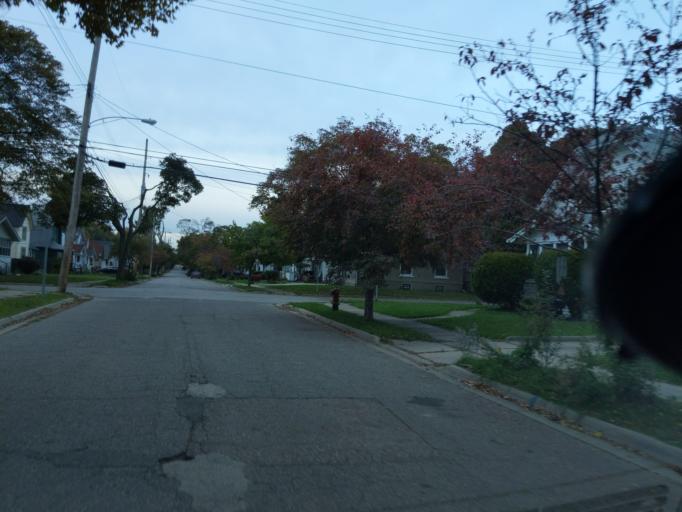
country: US
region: Michigan
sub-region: Ingham County
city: Lansing
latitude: 42.7357
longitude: -84.5200
